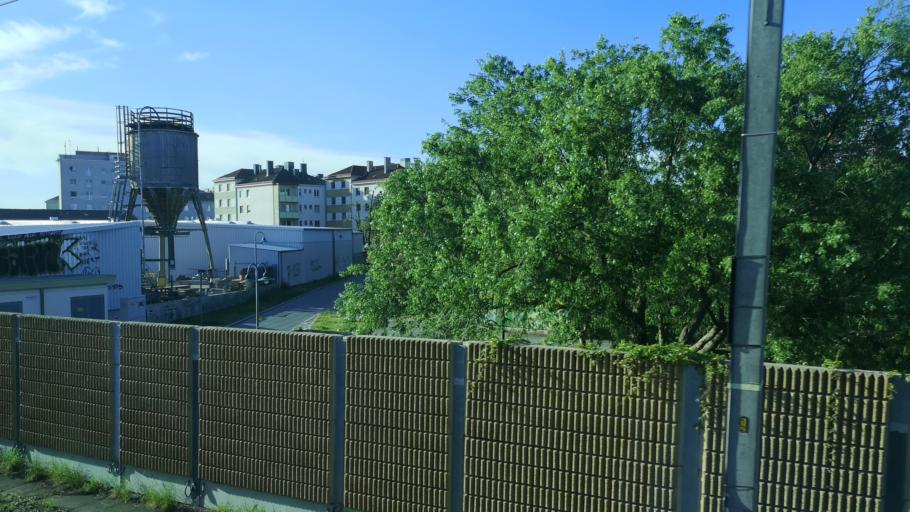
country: AT
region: Lower Austria
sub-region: Politischer Bezirk Wien-Umgebung
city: Schwechat
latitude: 48.1460
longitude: 16.4770
